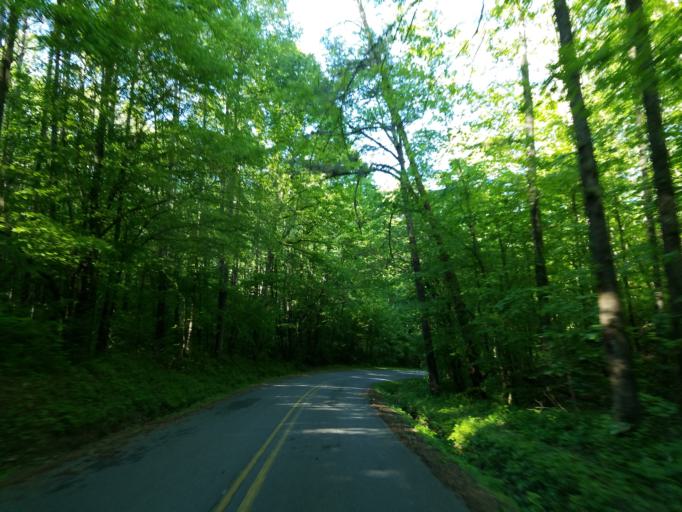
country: US
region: Georgia
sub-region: Gilmer County
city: Ellijay
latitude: 34.5707
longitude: -84.5164
